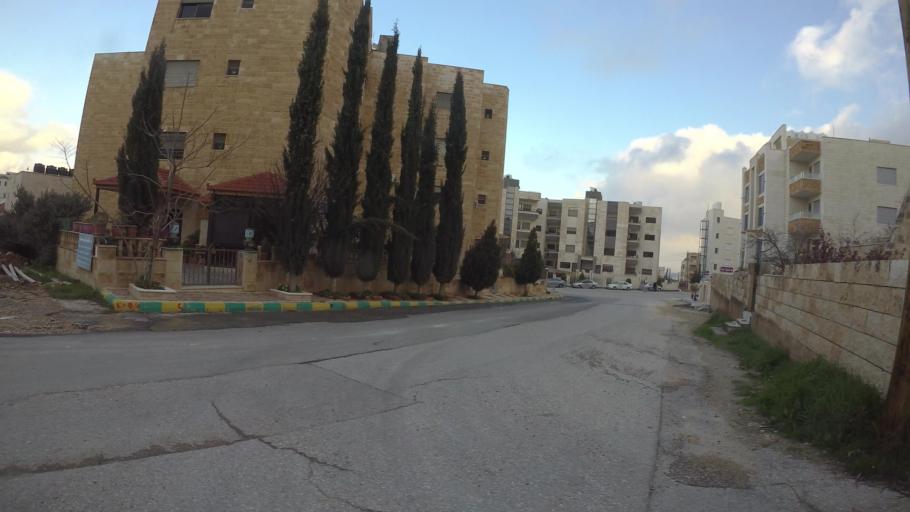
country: JO
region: Amman
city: Al Jubayhah
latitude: 32.0472
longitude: 35.8948
